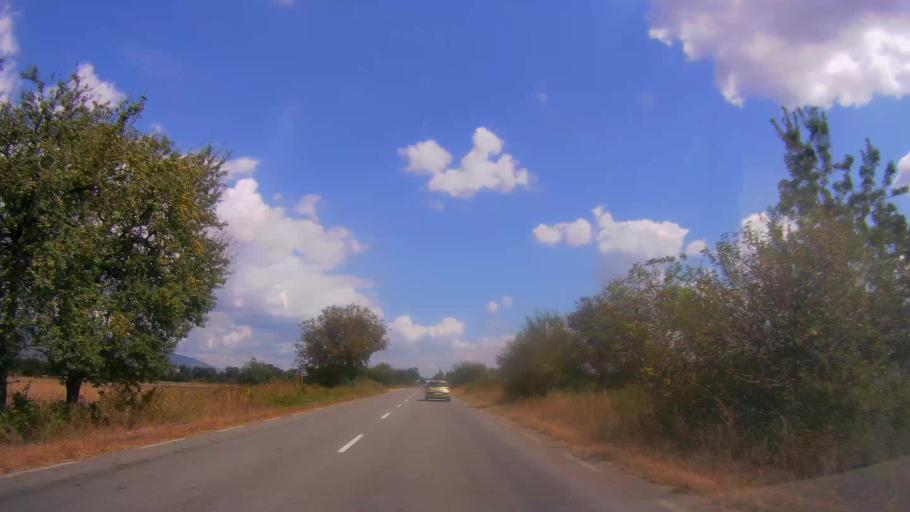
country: BG
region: Sliven
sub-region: Obshtina Tvurditsa
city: Tvurditsa
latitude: 42.6563
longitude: 25.8887
